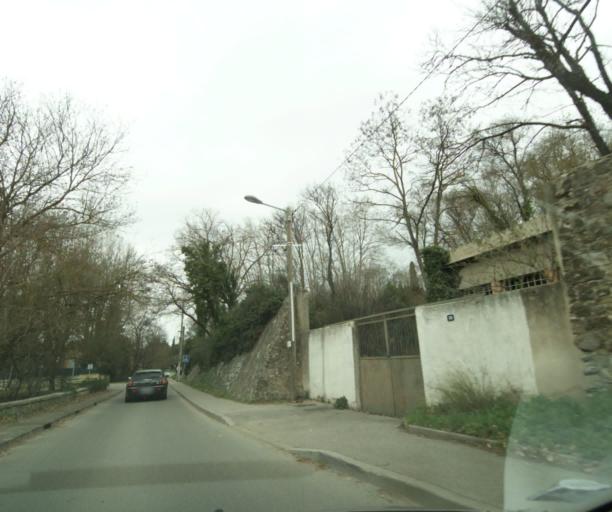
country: FR
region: Provence-Alpes-Cote d'Azur
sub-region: Departement des Bouches-du-Rhone
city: Aix-en-Provence
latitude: 43.5358
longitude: 5.4712
